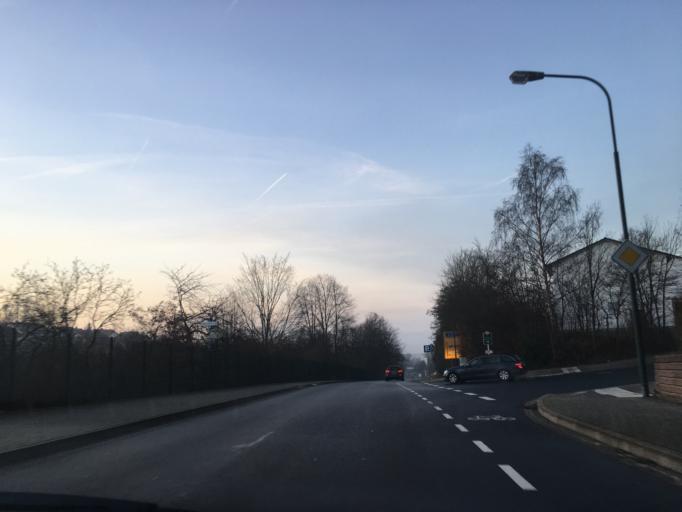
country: DE
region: Hesse
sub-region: Regierungsbezirk Kassel
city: Petersberg
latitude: 50.5609
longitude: 9.7019
